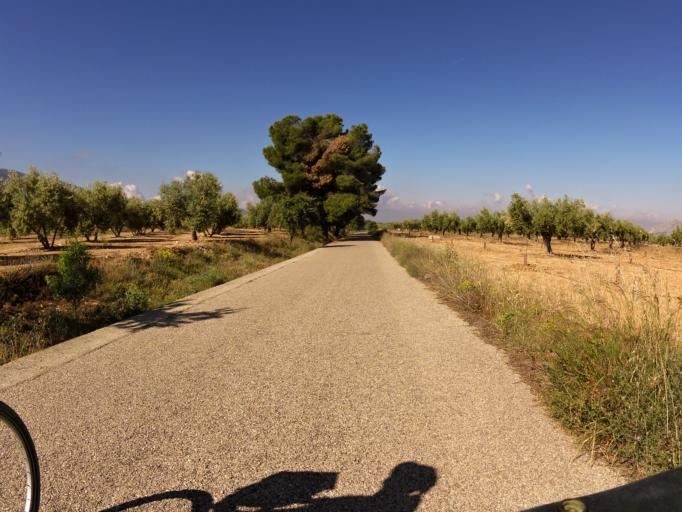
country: ES
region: Valencia
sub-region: Provincia de Alicante
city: Biar
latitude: 38.6360
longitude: -0.7838
